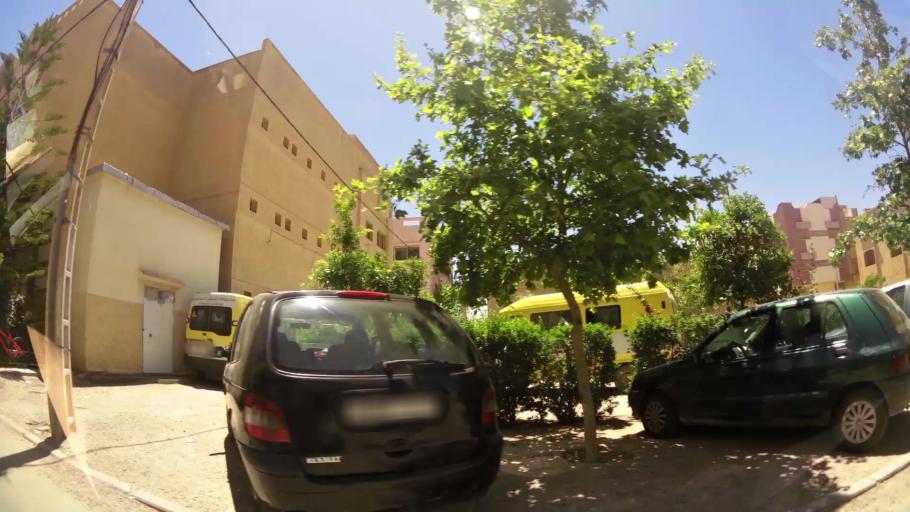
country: MA
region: Oriental
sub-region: Oujda-Angad
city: Oujda
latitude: 34.6757
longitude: -1.8804
